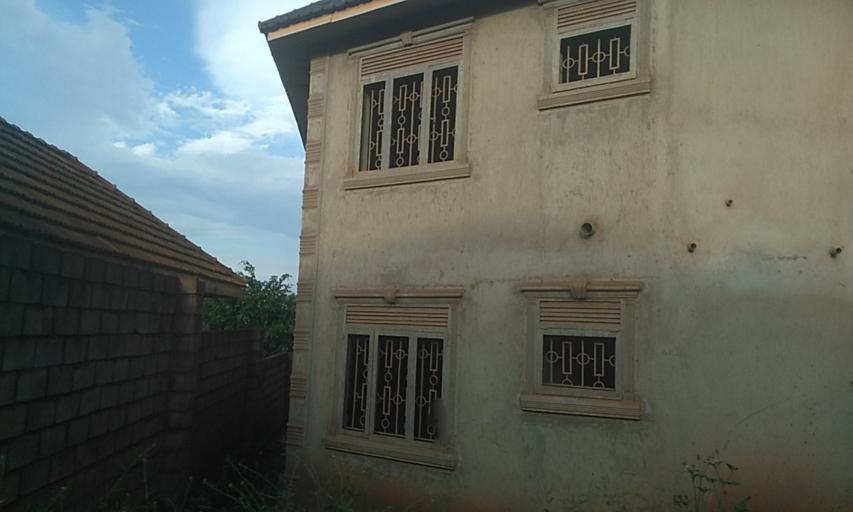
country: UG
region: Central Region
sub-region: Wakiso District
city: Kajansi
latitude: 0.2630
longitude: 32.5301
